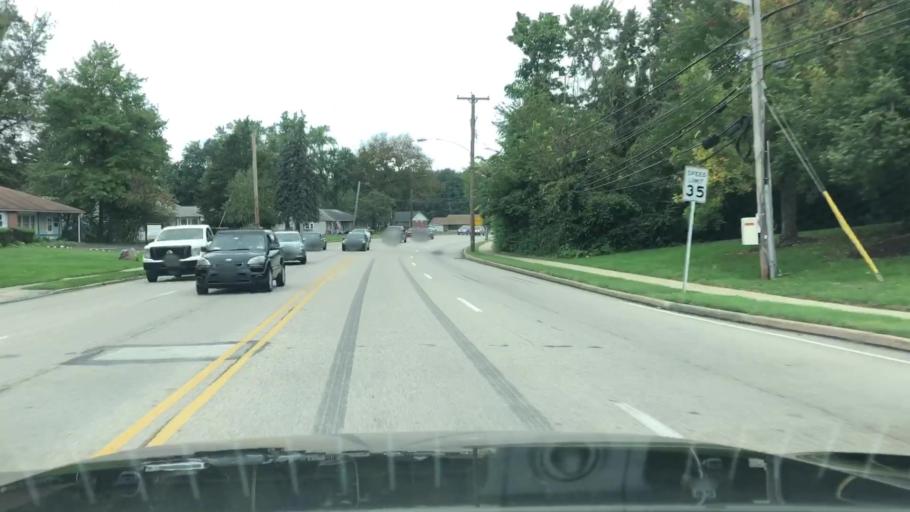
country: US
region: Pennsylvania
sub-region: Montgomery County
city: Plymouth Meeting
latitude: 40.1292
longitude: -75.3000
